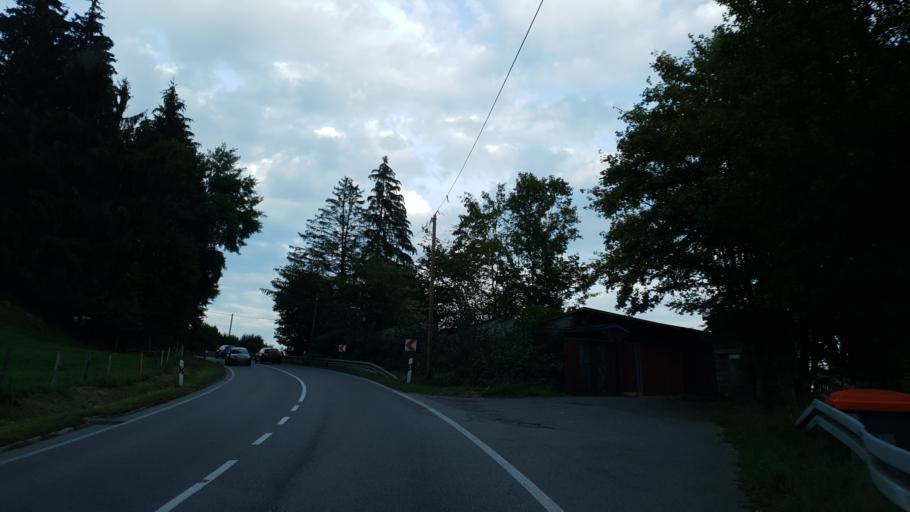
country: DE
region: Bavaria
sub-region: Swabia
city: Heimenkirch
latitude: 47.6591
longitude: 9.9358
